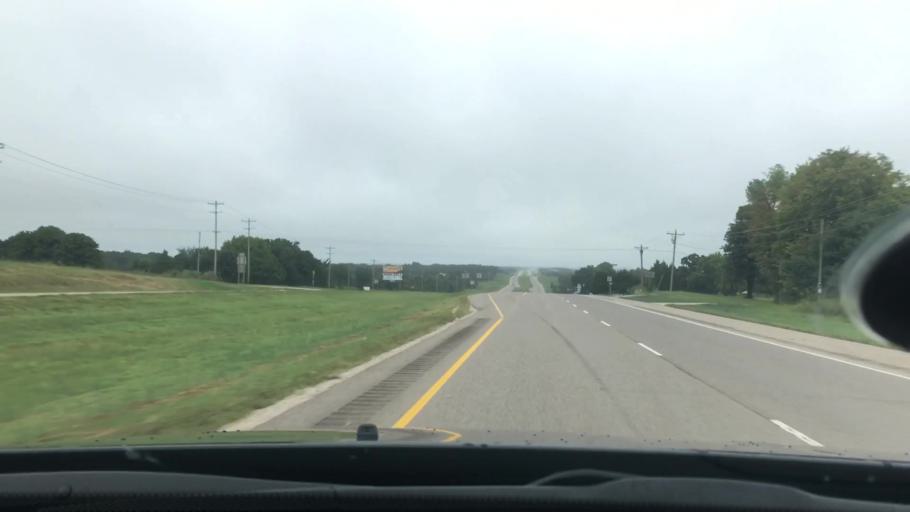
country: US
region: Oklahoma
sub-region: Seminole County
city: Seminole
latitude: 35.3175
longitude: -96.6713
